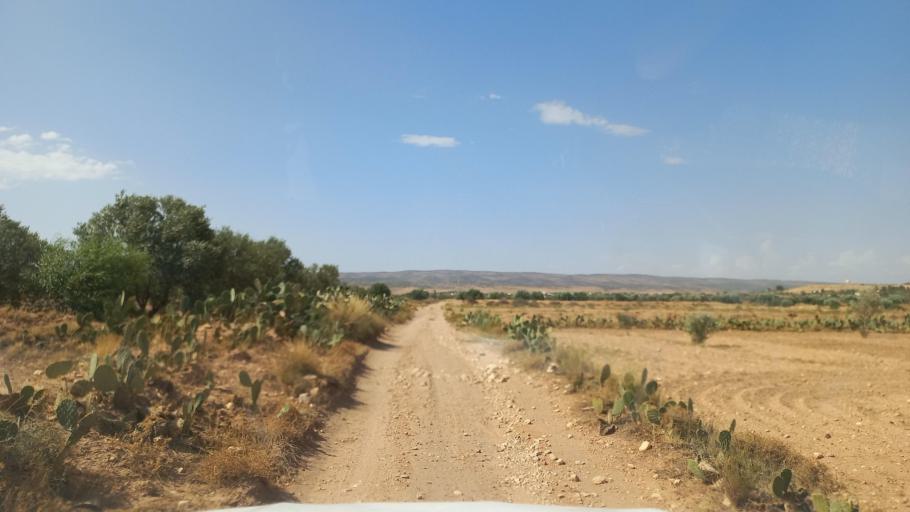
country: TN
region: Al Qasrayn
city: Kasserine
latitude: 35.2597
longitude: 8.9513
